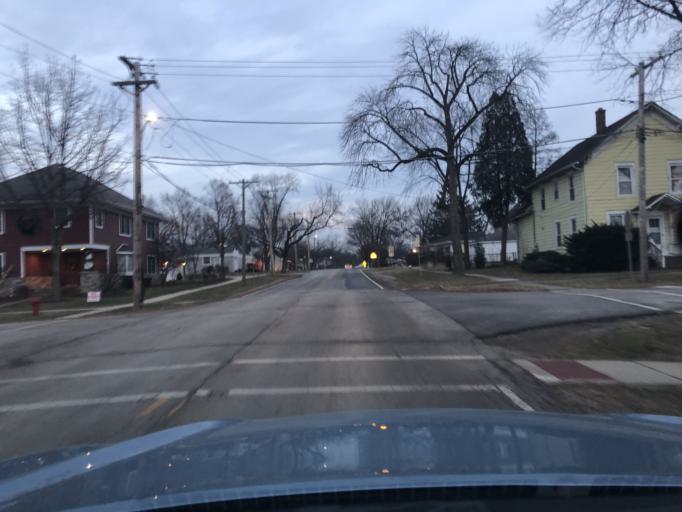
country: US
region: Illinois
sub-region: DuPage County
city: Itasca
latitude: 41.9743
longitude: -88.0122
